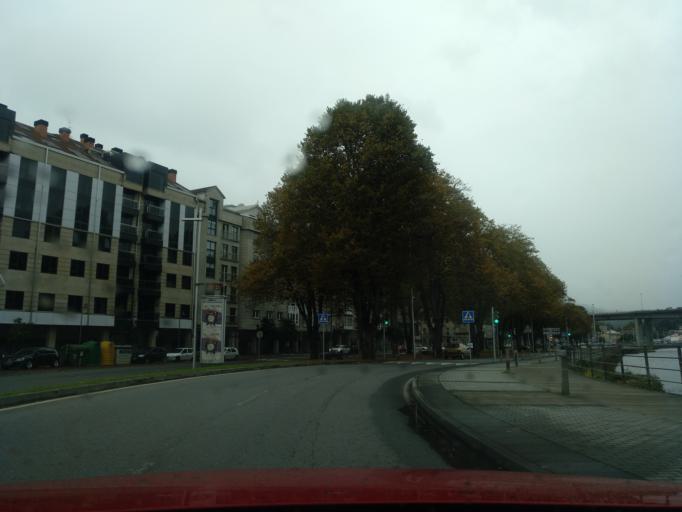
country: ES
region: Galicia
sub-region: Provincia de Pontevedra
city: Pontevedra
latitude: 42.4283
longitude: -8.6518
